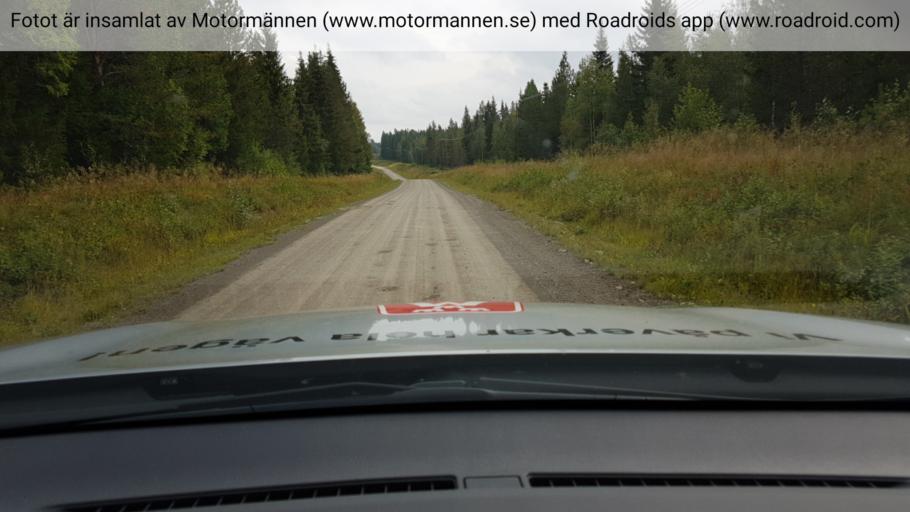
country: SE
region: Jaemtland
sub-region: Stroemsunds Kommun
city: Stroemsund
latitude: 63.7611
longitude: 15.3526
